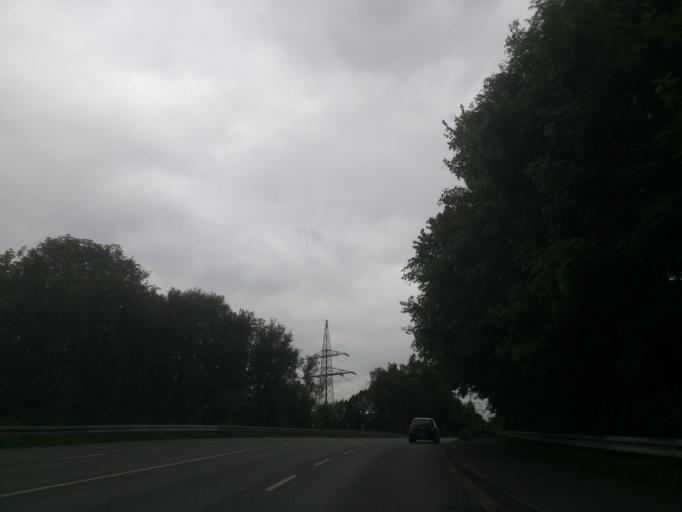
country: DE
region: North Rhine-Westphalia
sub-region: Regierungsbezirk Detmold
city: Paderborn
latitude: 51.7100
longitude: 8.7194
